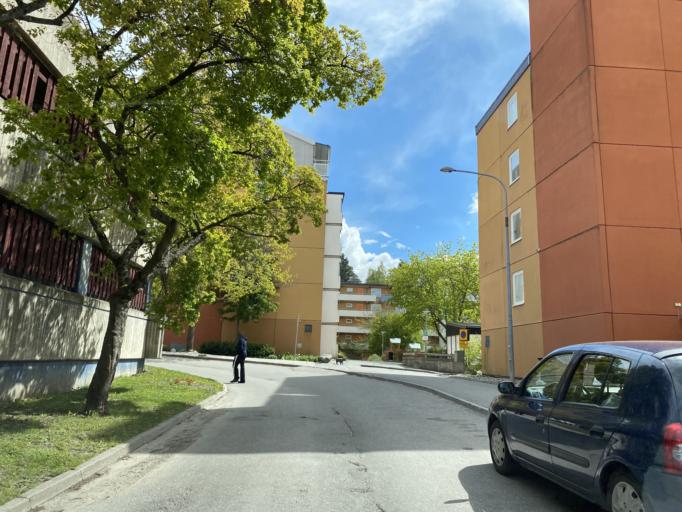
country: SE
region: Stockholm
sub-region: Stockholms Kommun
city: Kista
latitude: 59.4070
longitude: 17.9235
